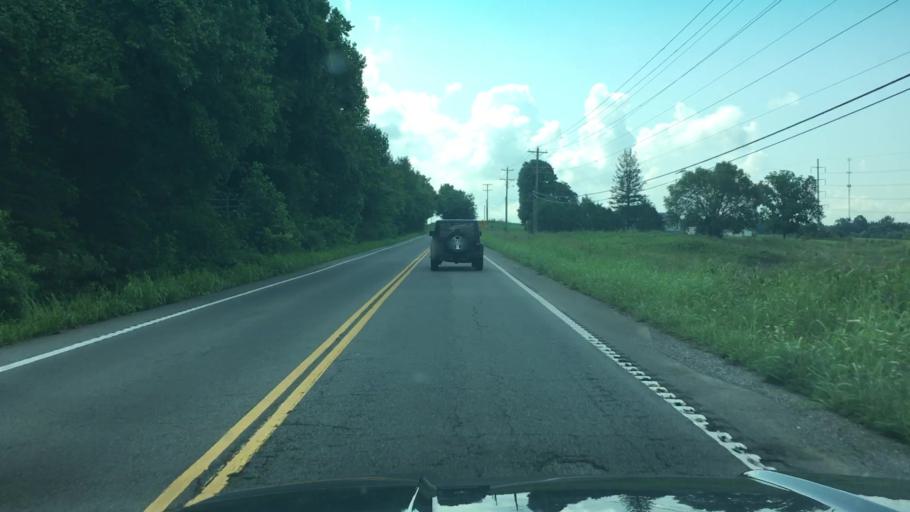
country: US
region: Tennessee
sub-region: Williamson County
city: Nolensville
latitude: 35.8640
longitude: -86.6877
